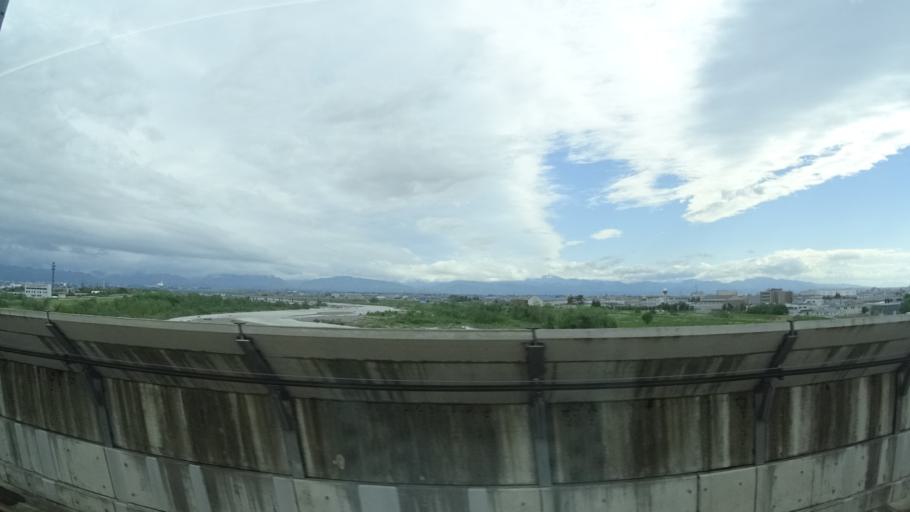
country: JP
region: Toyama
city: Toyama-shi
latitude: 36.7144
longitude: 137.2728
